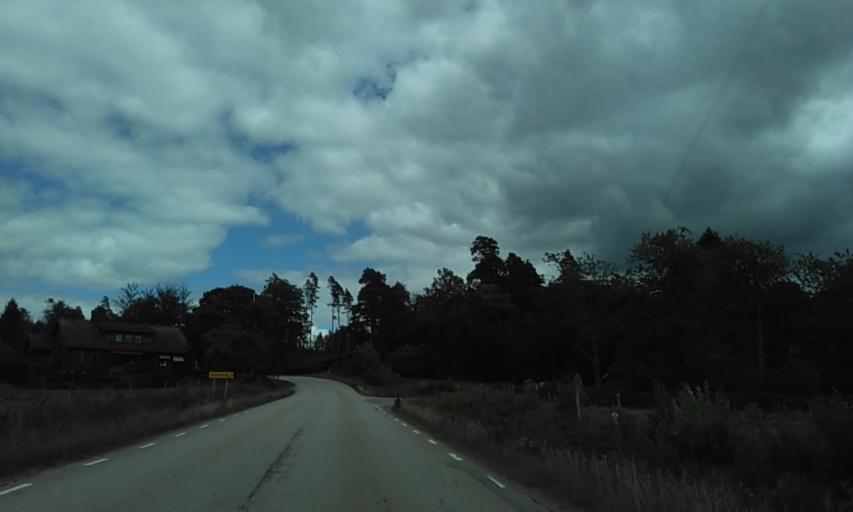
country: SE
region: Vaestra Goetaland
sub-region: Boras Kommun
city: Boras
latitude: 57.8131
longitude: 12.9203
